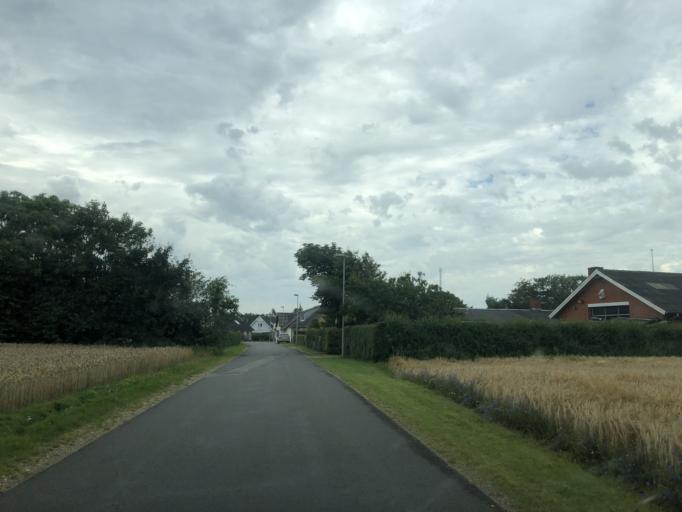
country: DK
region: Central Jutland
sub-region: Holstebro Kommune
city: Holstebro
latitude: 56.3780
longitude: 8.5226
